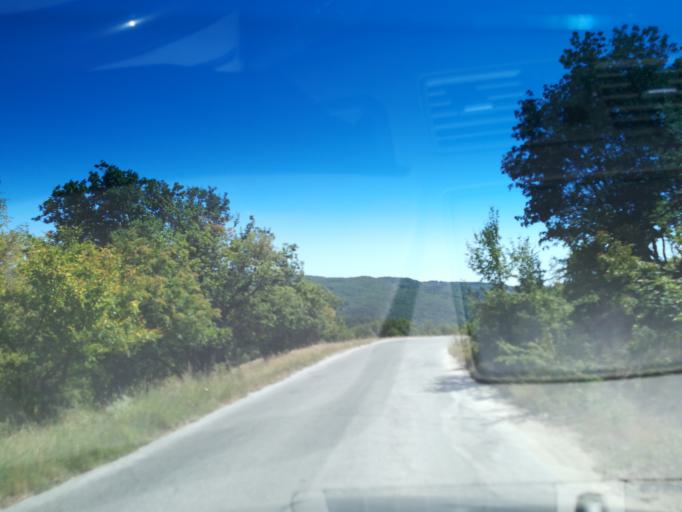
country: BG
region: Pazardzhik
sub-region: Obshtina Strelcha
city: Strelcha
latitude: 42.5448
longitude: 24.3298
